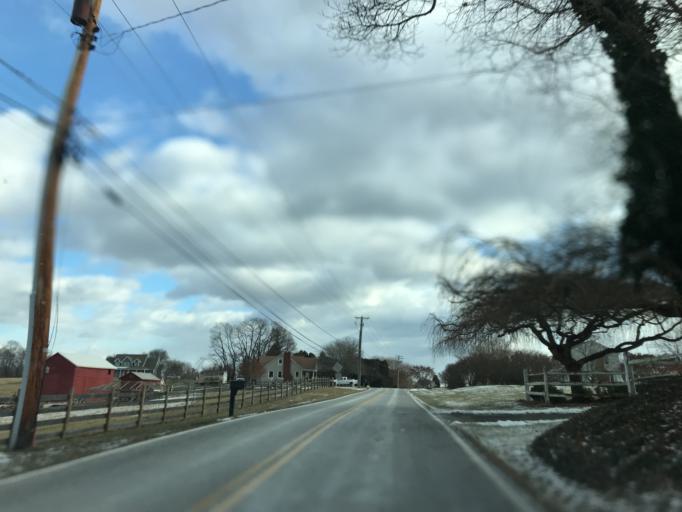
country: US
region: Maryland
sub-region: Harford County
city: Jarrettsville
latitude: 39.6150
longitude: -76.4492
